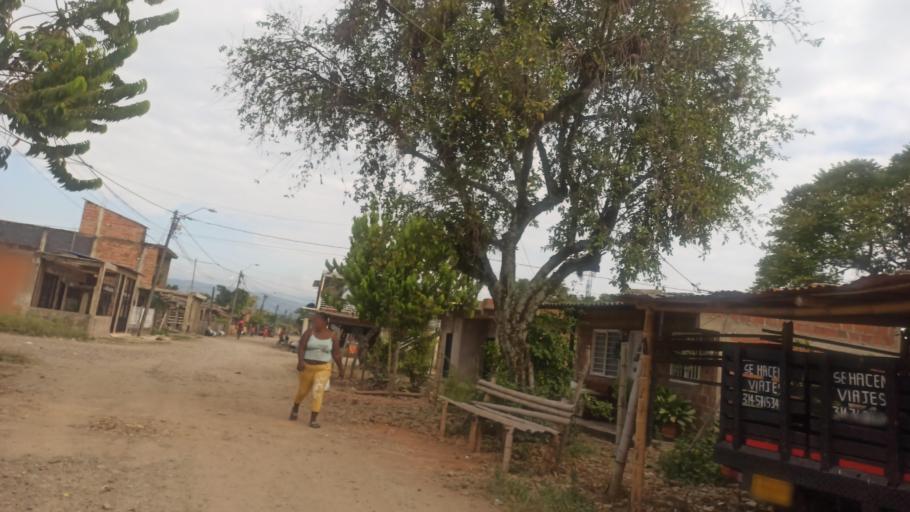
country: CO
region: Valle del Cauca
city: Jamundi
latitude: 3.1273
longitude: -76.5574
